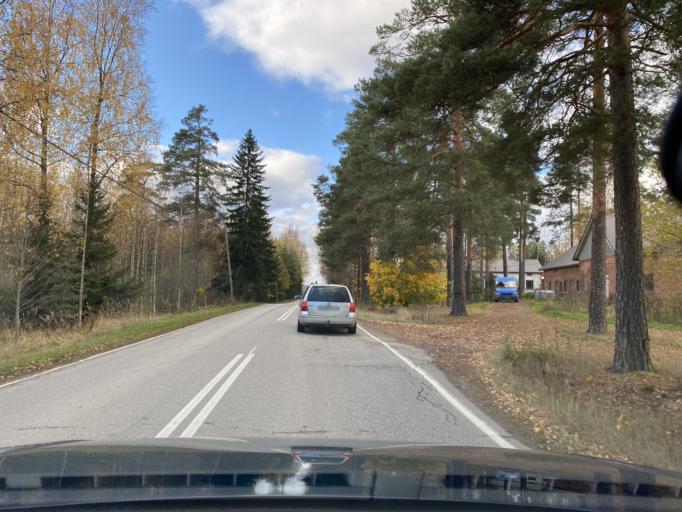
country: FI
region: Pirkanmaa
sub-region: Lounais-Pirkanmaa
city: Punkalaidun
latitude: 61.0417
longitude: 23.2118
